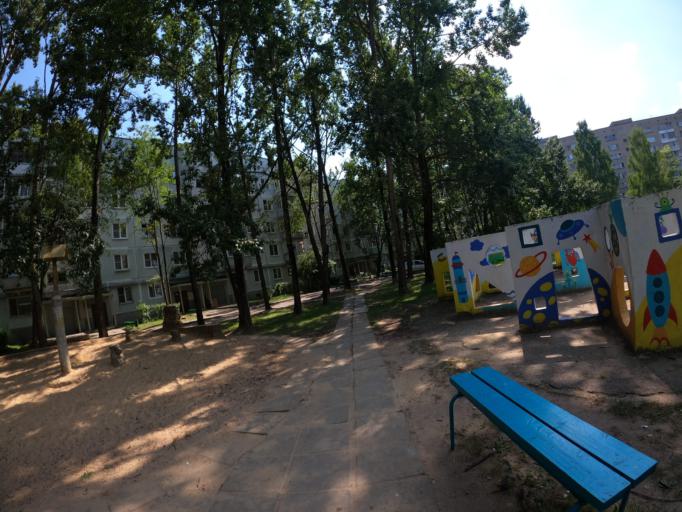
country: RU
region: Kaluga
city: Obninsk
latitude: 55.1134
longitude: 36.5940
